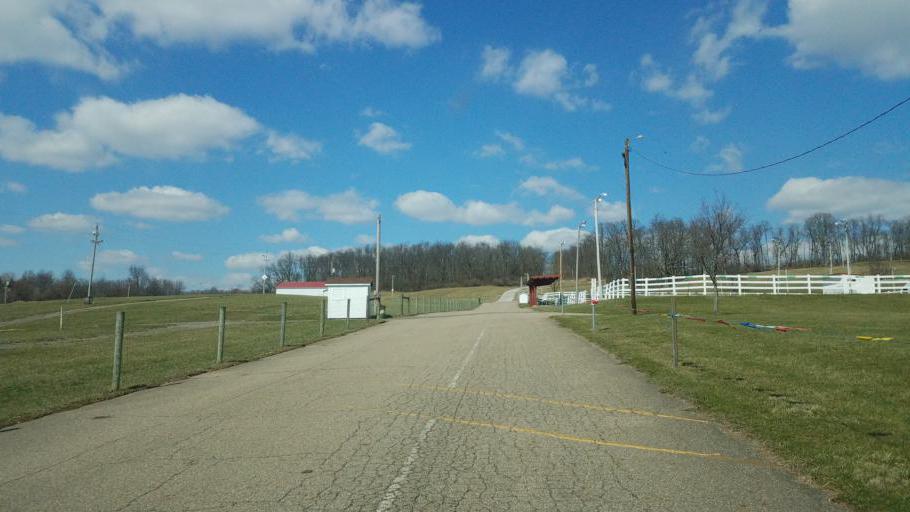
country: US
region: Ohio
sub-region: Knox County
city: Mount Vernon
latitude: 40.4176
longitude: -82.4759
